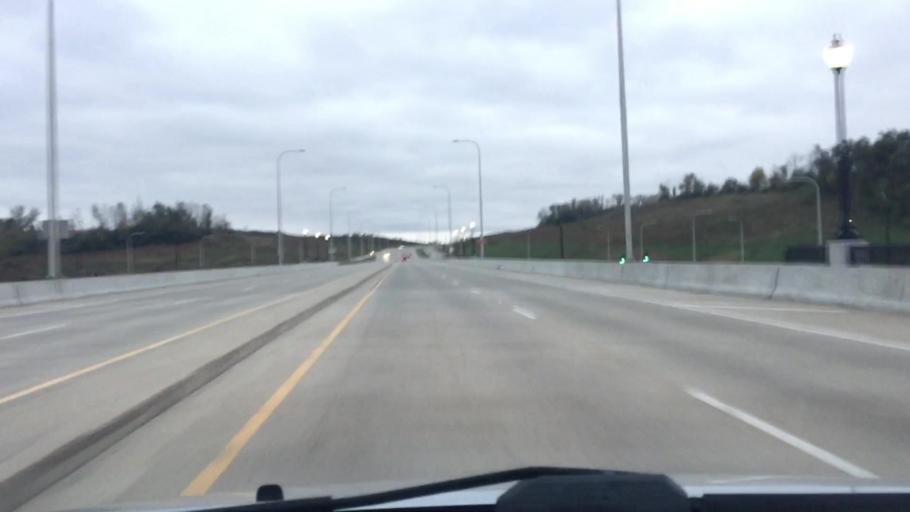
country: US
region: Illinois
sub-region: McHenry County
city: Algonquin
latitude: 42.1685
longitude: -88.2969
